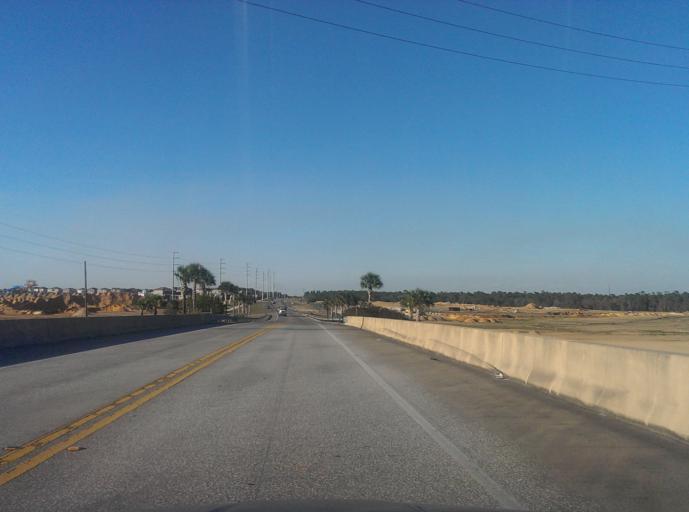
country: US
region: Florida
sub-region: Polk County
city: Loughman
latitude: 28.2855
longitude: -81.5904
